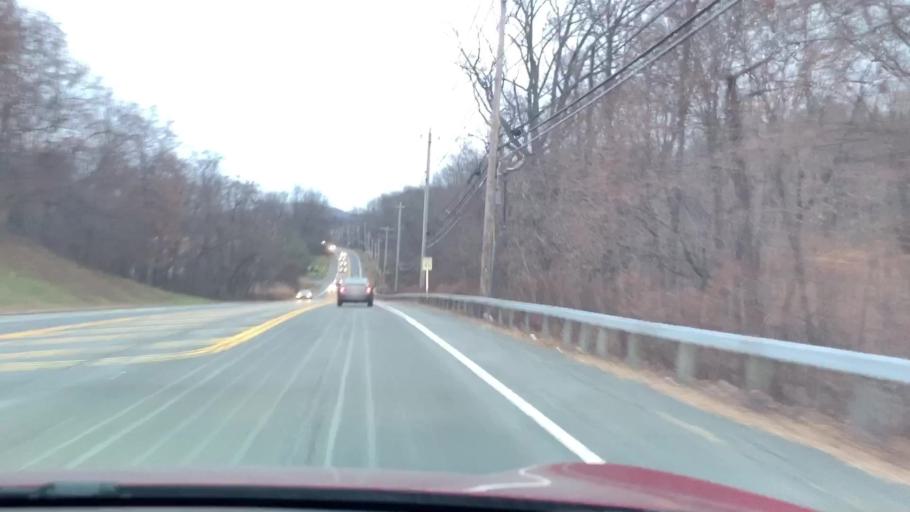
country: US
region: New York
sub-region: Rockland County
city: Sparkill
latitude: 41.0190
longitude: -73.9155
